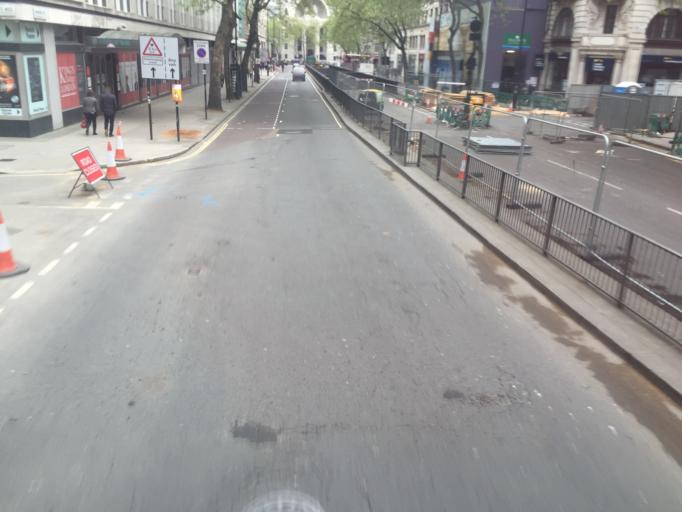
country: GB
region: England
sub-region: Greater London
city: London
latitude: 51.5151
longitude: -0.1187
